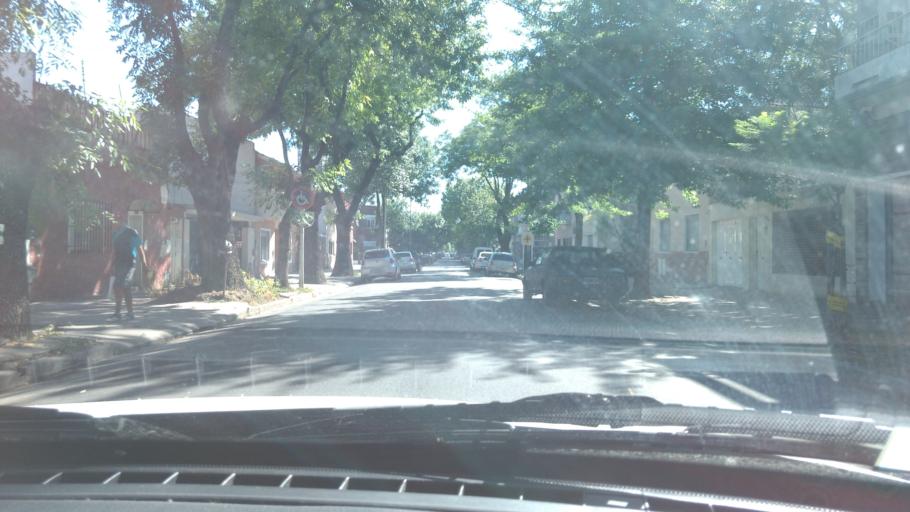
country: AR
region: Buenos Aires F.D.
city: Villa Santa Rita
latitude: -34.6105
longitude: -58.5103
